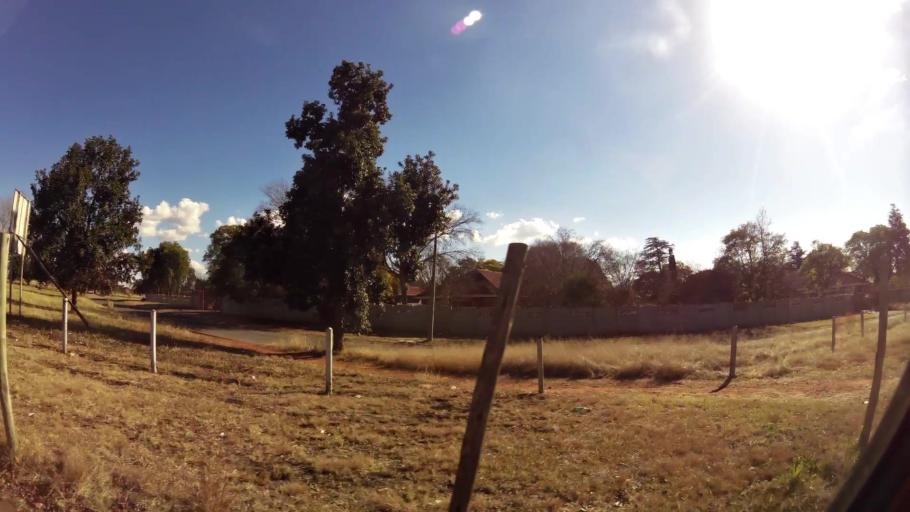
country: ZA
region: Gauteng
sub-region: West Rand District Municipality
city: Carletonville
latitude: -26.3735
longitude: 27.4062
